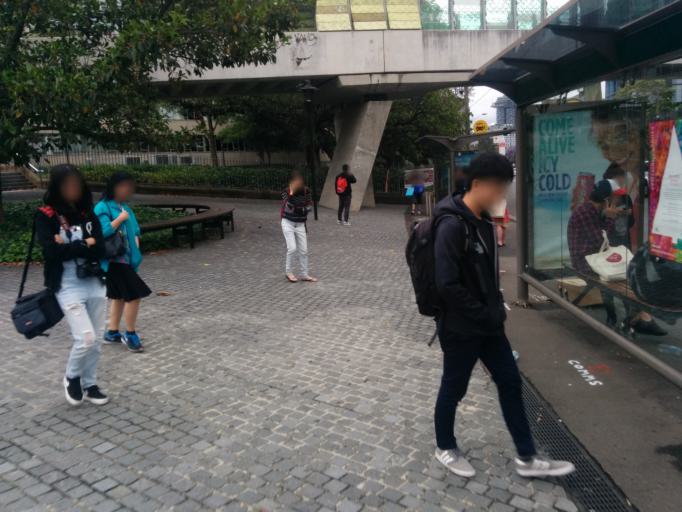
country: AU
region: New South Wales
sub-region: City of Sydney
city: Darlington
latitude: -33.8892
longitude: 151.1902
